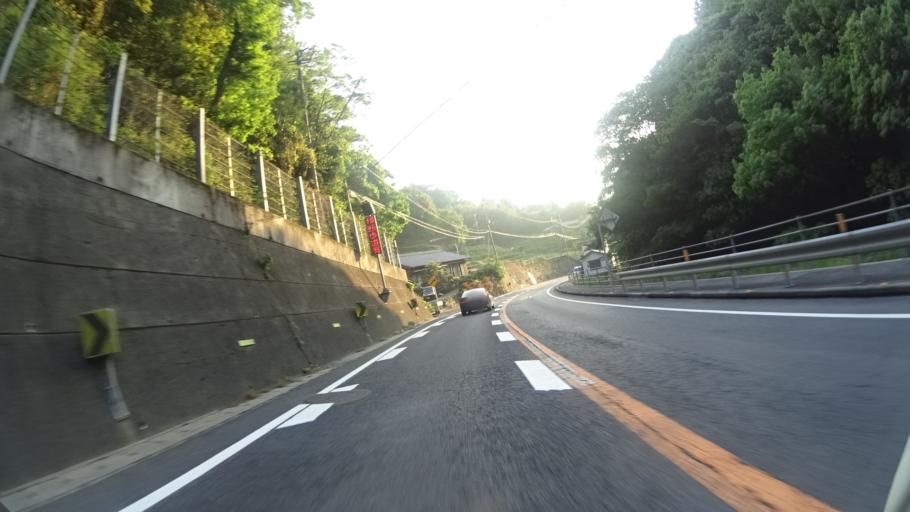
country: JP
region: Ehime
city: Kawanoecho
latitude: 33.9959
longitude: 133.6659
